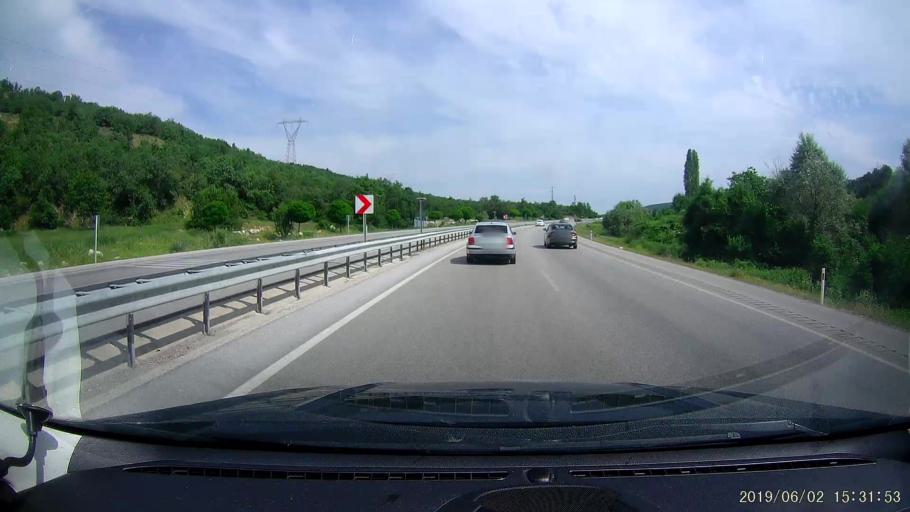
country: TR
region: Amasya
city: Saraycik
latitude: 40.9436
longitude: 35.1336
